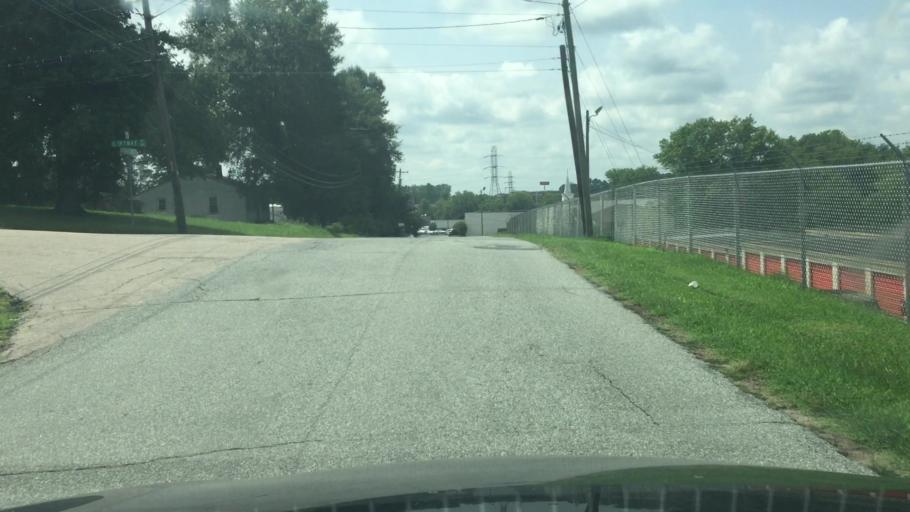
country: US
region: North Carolina
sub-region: Cabarrus County
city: Kannapolis
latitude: 35.4535
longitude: -80.6071
